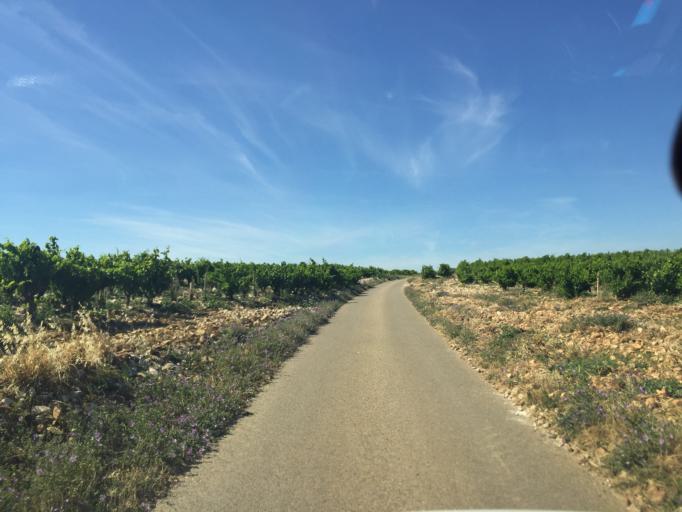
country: FR
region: Provence-Alpes-Cote d'Azur
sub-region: Departement du Vaucluse
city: Chateauneuf-du-Pape
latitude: 44.0692
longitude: 4.8065
